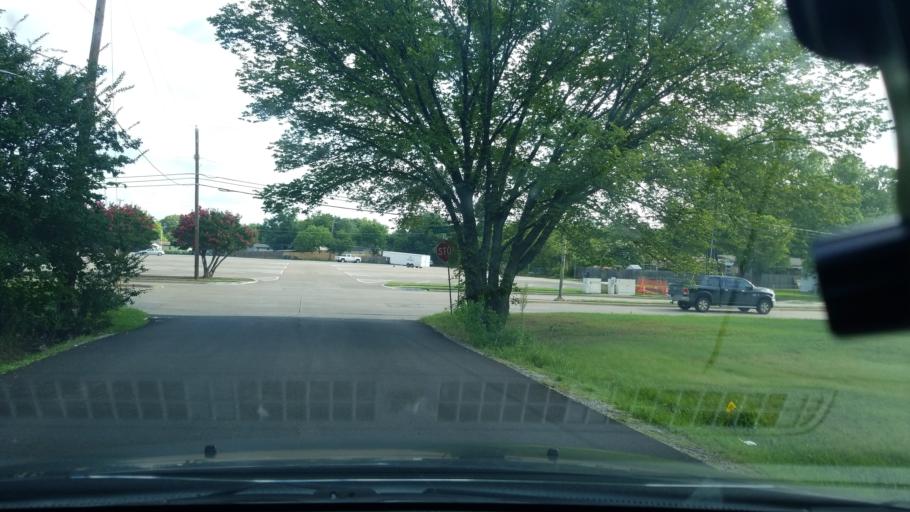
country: US
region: Texas
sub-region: Dallas County
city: Mesquite
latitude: 32.8211
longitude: -96.6636
